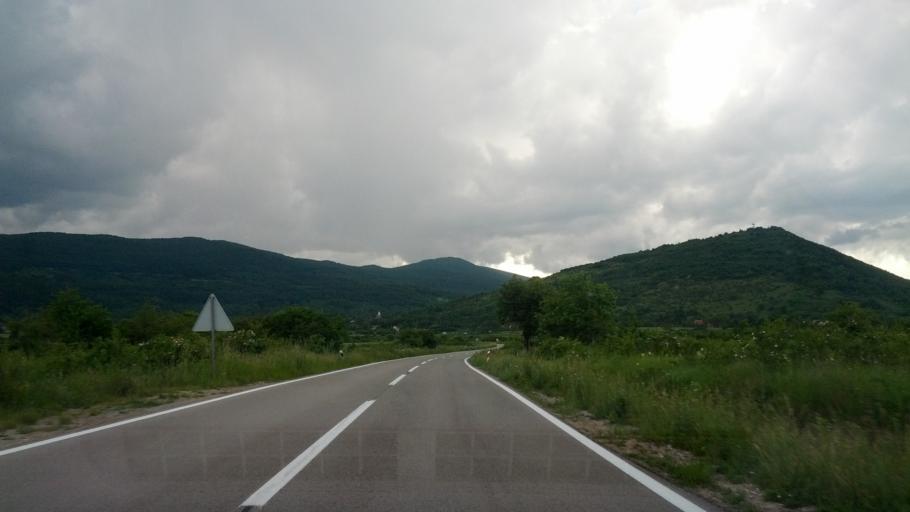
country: BA
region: Federation of Bosnia and Herzegovina
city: Izacic
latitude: 44.8787
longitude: 15.7410
